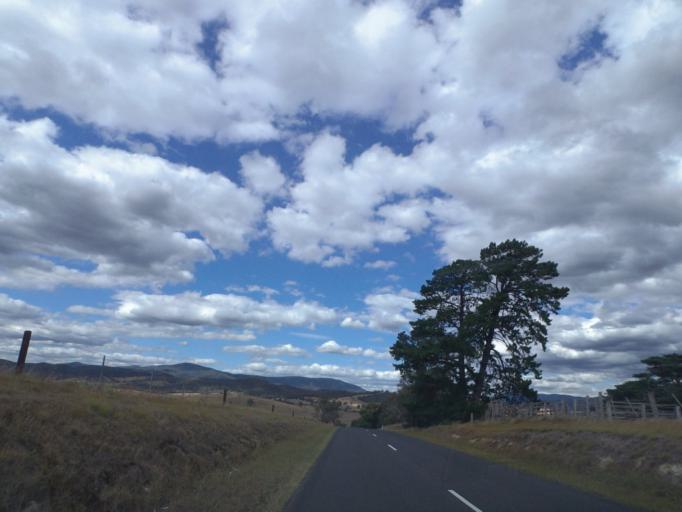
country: AU
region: Victoria
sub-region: Yarra Ranges
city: Yarra Glen
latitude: -37.6395
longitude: 145.4262
